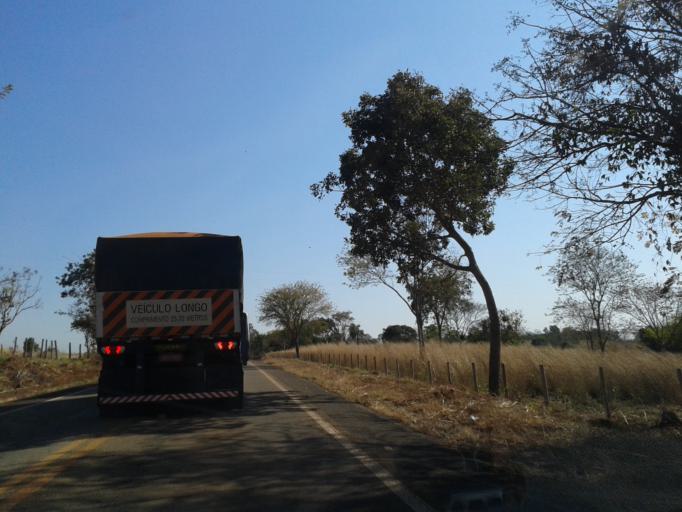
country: BR
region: Goias
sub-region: Mozarlandia
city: Mozarlandia
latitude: -14.7396
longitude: -50.5435
